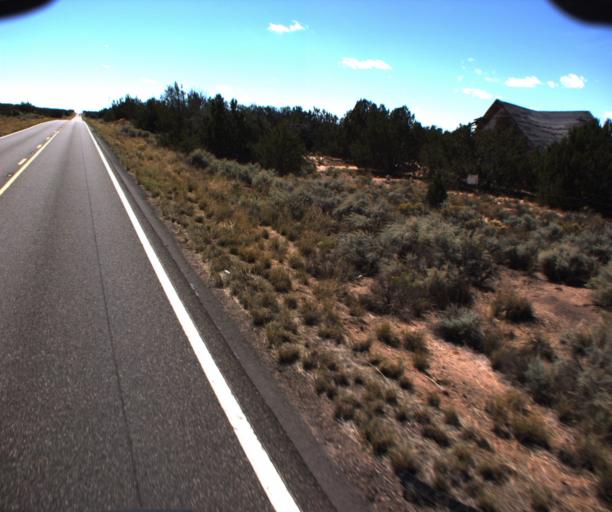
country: US
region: Arizona
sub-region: Apache County
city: Saint Johns
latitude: 34.8605
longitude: -109.2378
